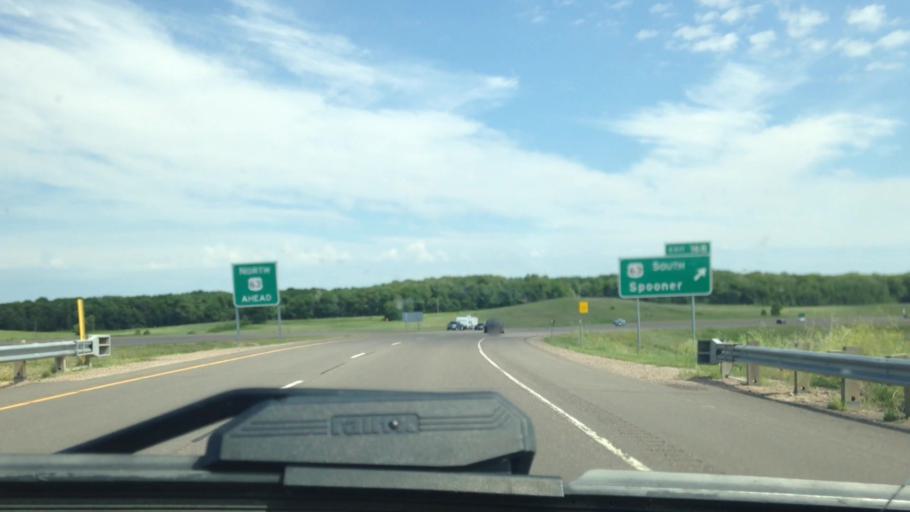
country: US
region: Wisconsin
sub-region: Washburn County
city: Spooner
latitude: 45.8526
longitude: -91.8598
